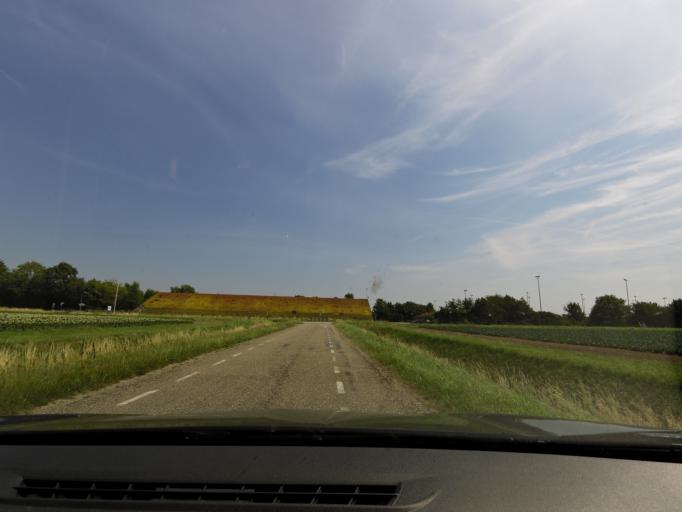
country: NL
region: South Holland
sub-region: Gemeente Binnenmaas
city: Mijnsheerenland
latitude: 51.8019
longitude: 4.5160
